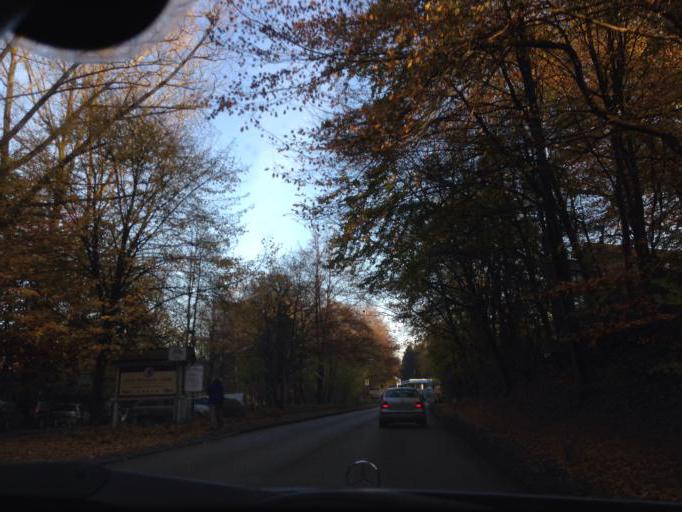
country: DE
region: Schleswig-Holstein
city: Aumuhle
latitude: 53.5309
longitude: 10.3091
